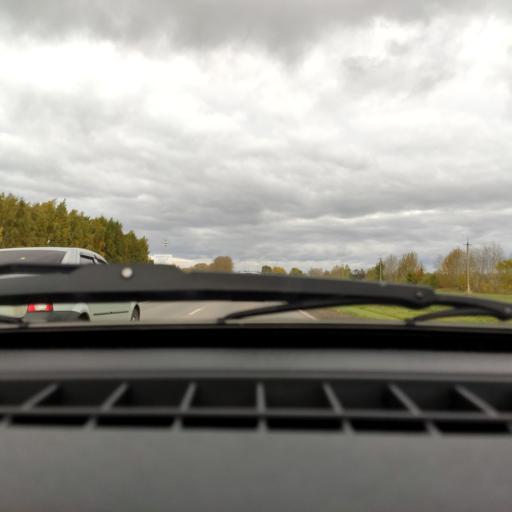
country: RU
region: Bashkortostan
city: Rayevskiy
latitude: 54.0273
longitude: 54.8970
